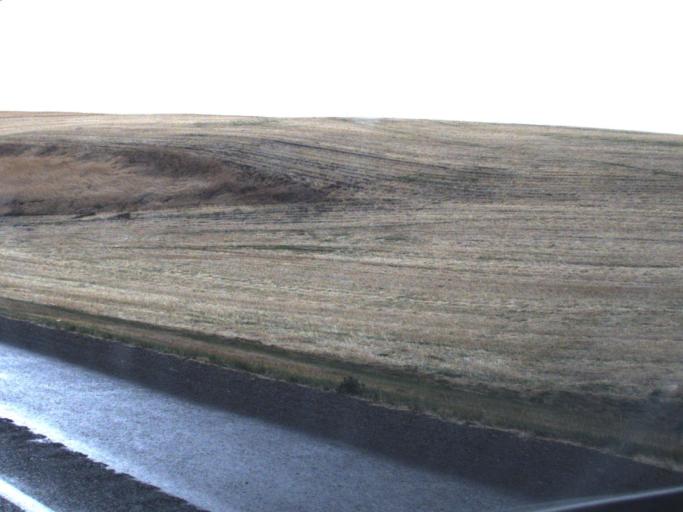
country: US
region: Washington
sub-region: Asotin County
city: Clarkston
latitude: 46.5515
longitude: -117.1010
